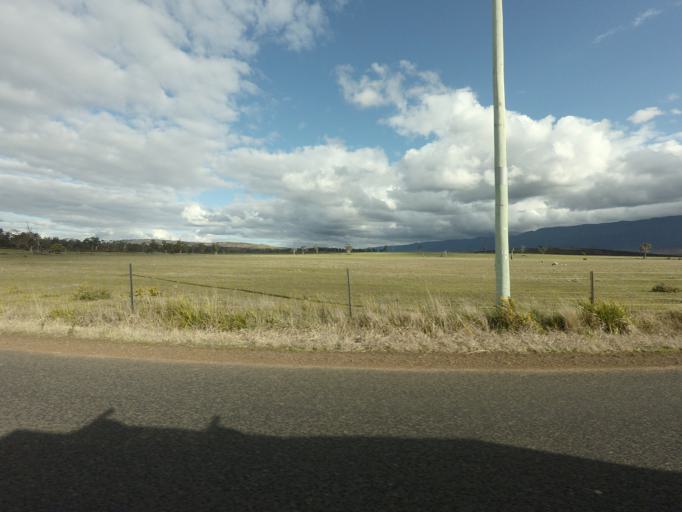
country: AU
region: Tasmania
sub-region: Northern Midlands
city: Longford
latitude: -41.8614
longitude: 147.2566
